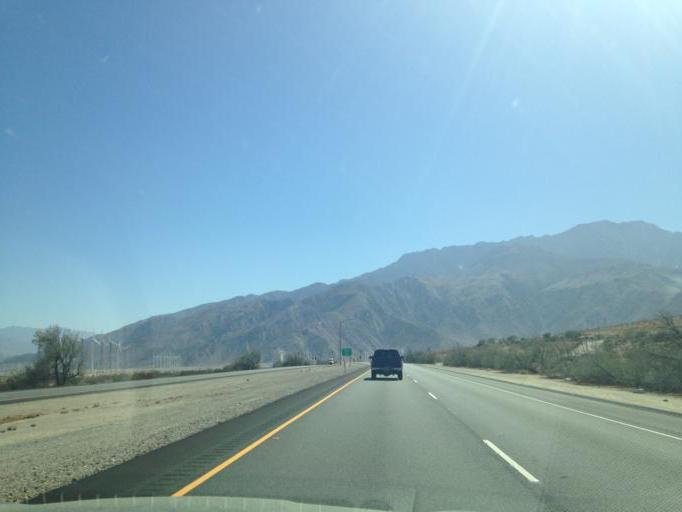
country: US
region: California
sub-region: Riverside County
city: Garnet
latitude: 33.9291
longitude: -116.5994
